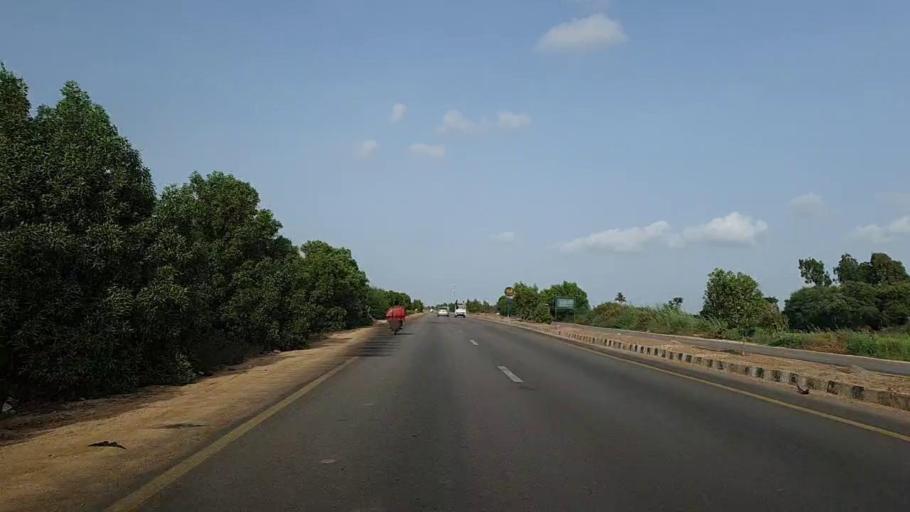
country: PK
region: Sindh
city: Thatta
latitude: 24.7435
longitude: 67.8366
